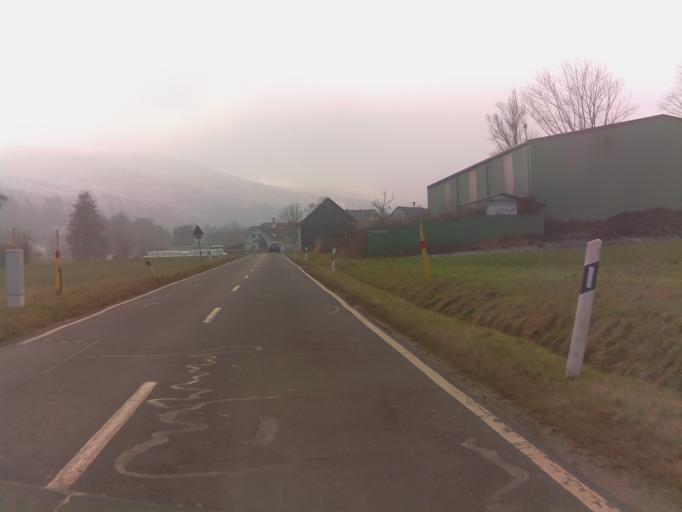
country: DE
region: Hesse
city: Lutzelbach
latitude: 49.7625
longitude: 8.7716
